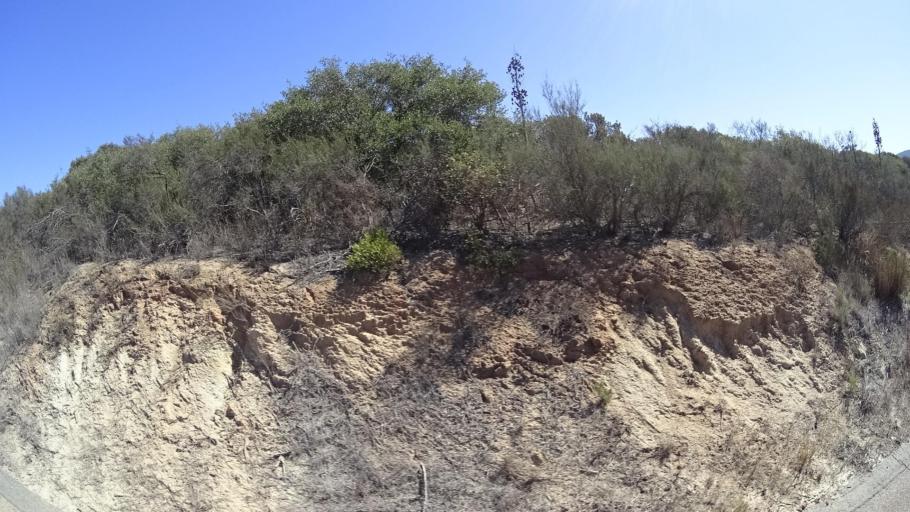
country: US
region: California
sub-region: San Diego County
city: Harbison Canyon
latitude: 32.7937
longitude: -116.8031
